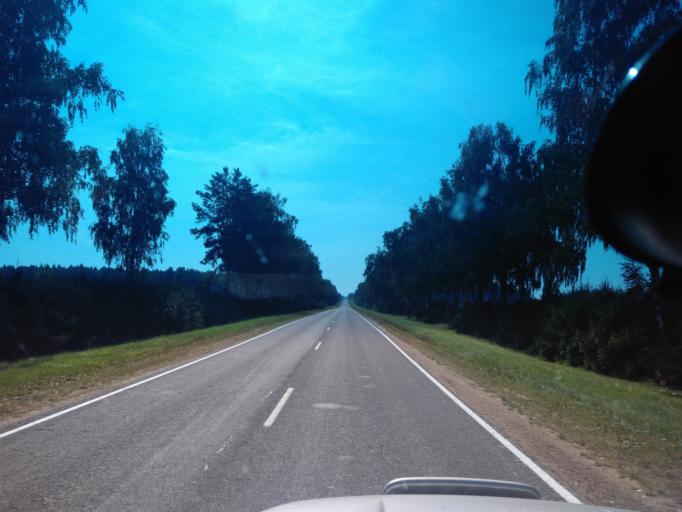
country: BY
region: Minsk
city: Uzda
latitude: 53.3466
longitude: 27.2272
